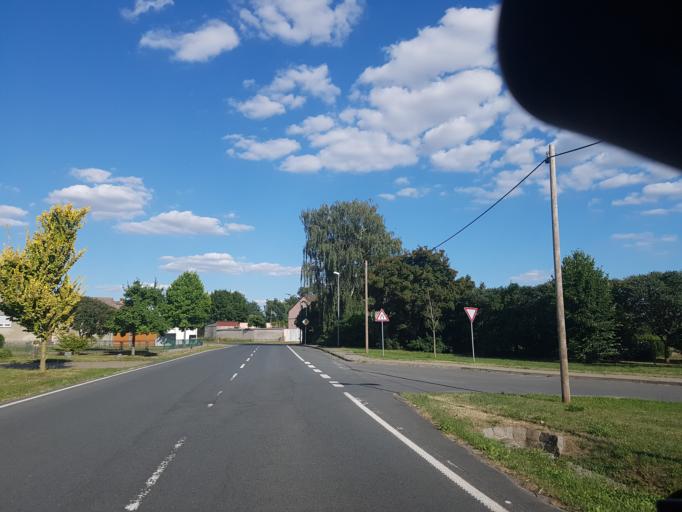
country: DE
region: Brandenburg
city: Juterbog
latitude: 51.9294
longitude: 13.1380
